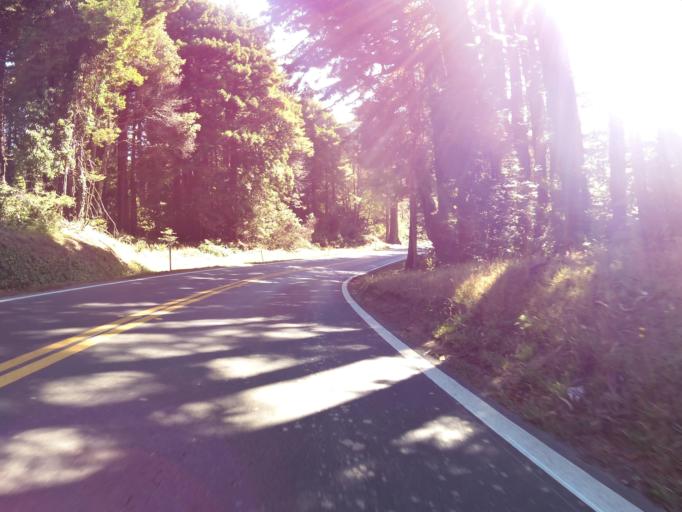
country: US
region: California
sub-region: Mendocino County
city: Fort Bragg
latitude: 39.5282
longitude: -123.7592
